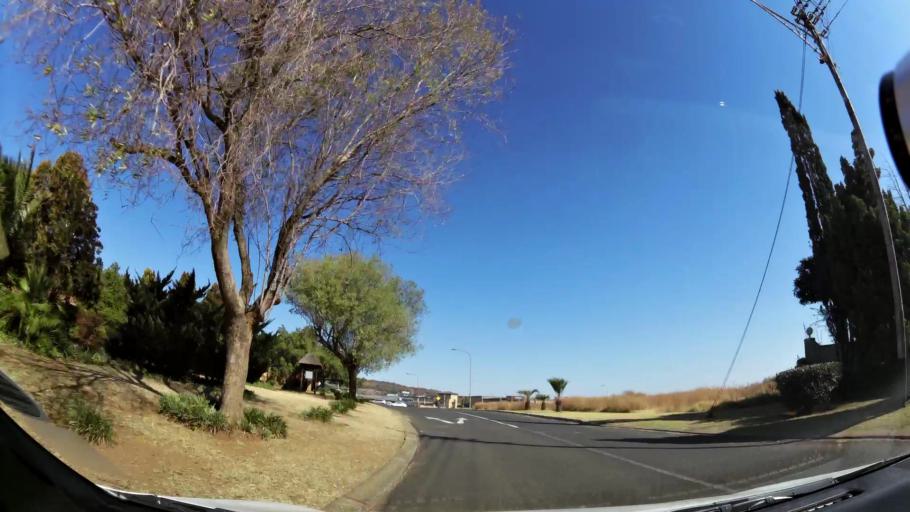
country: ZA
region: Gauteng
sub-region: City of Johannesburg Metropolitan Municipality
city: Johannesburg
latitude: -26.2709
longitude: 28.0301
